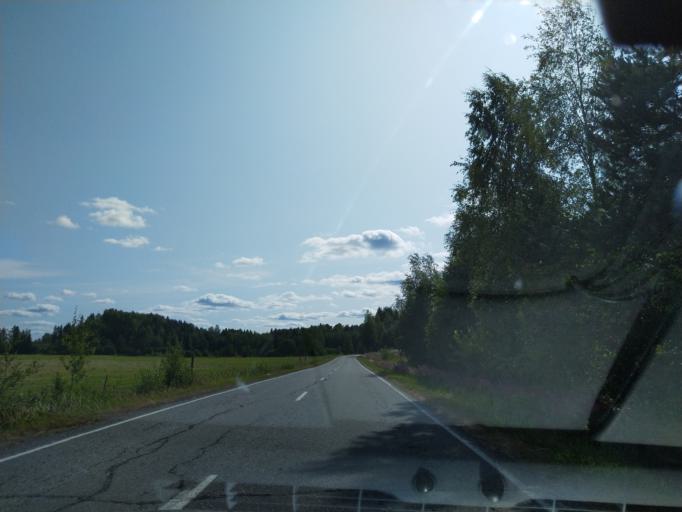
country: FI
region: Uusimaa
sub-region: Helsinki
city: Karkkila
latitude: 60.6150
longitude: 24.2802
